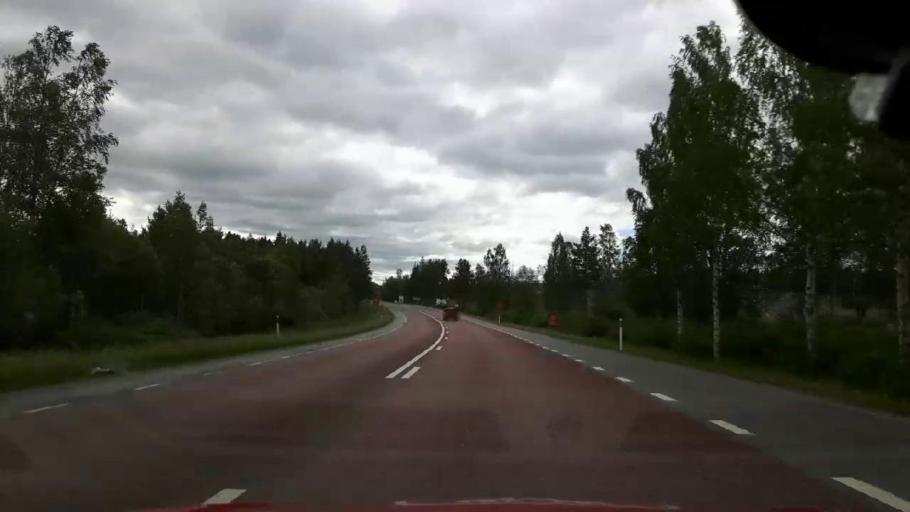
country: SE
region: Jaemtland
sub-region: Braecke Kommun
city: Braecke
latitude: 62.7602
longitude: 15.4096
